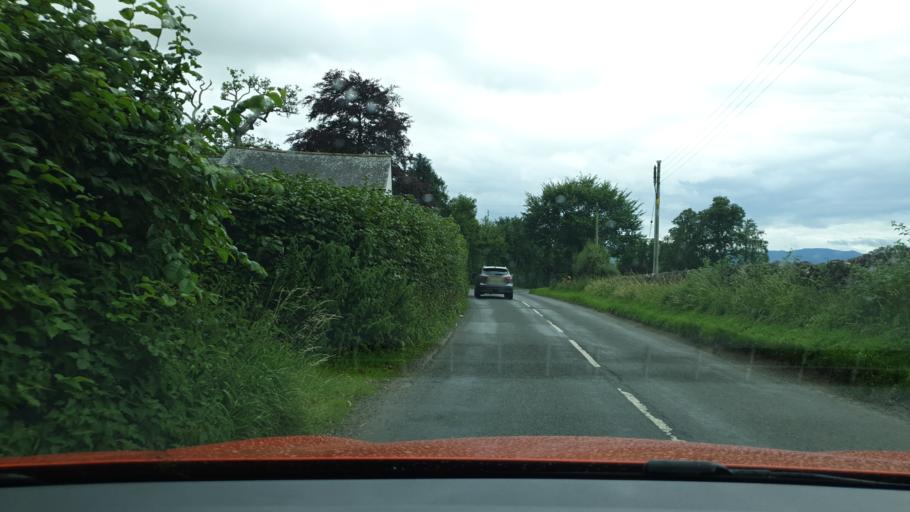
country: GB
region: England
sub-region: Cumbria
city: Penrith
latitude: 54.6167
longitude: -2.8106
